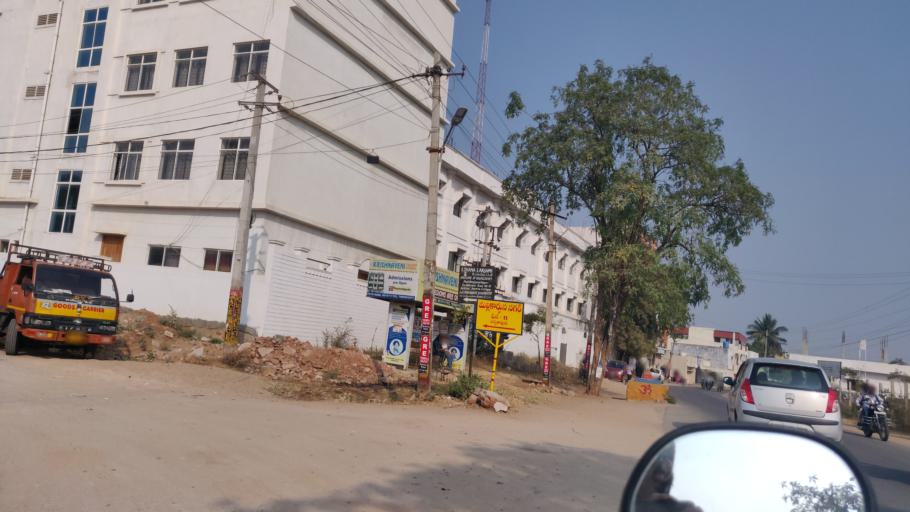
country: IN
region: Telangana
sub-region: Rangareddi
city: Uppal Kalan
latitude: 17.3912
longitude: 78.6035
